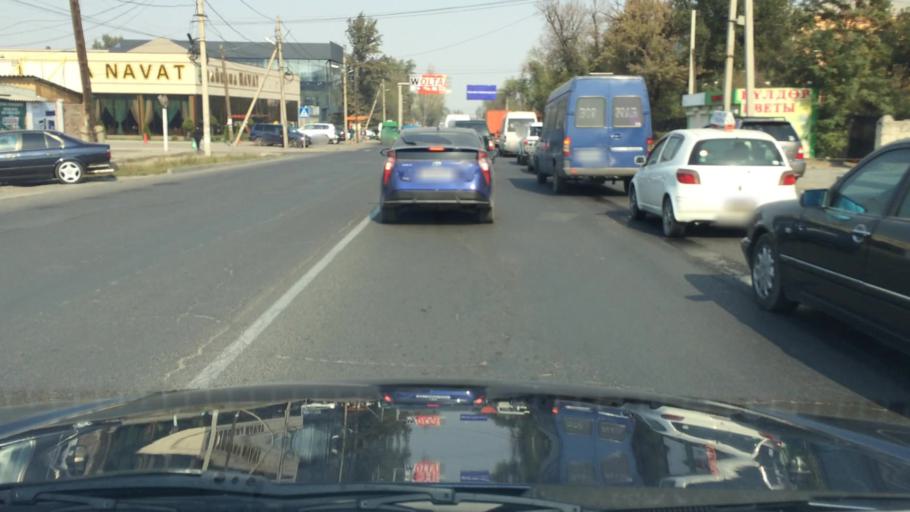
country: KG
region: Chuy
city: Lebedinovka
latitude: 42.8813
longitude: 74.6370
